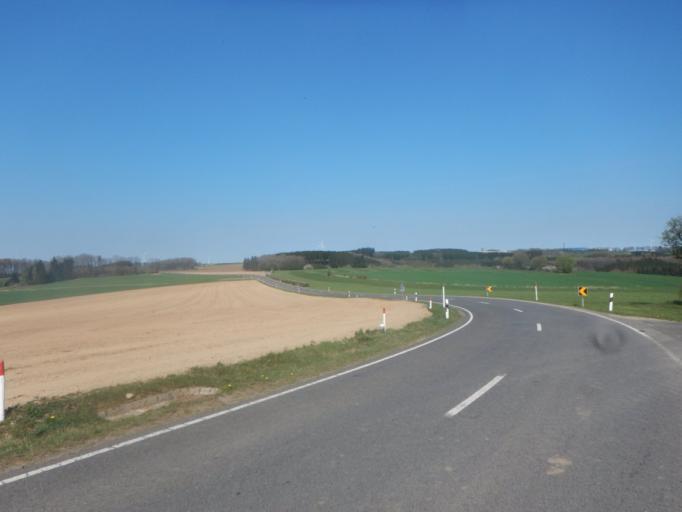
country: LU
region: Diekirch
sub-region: Canton de Clervaux
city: Clervaux
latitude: 50.0425
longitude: 5.9897
